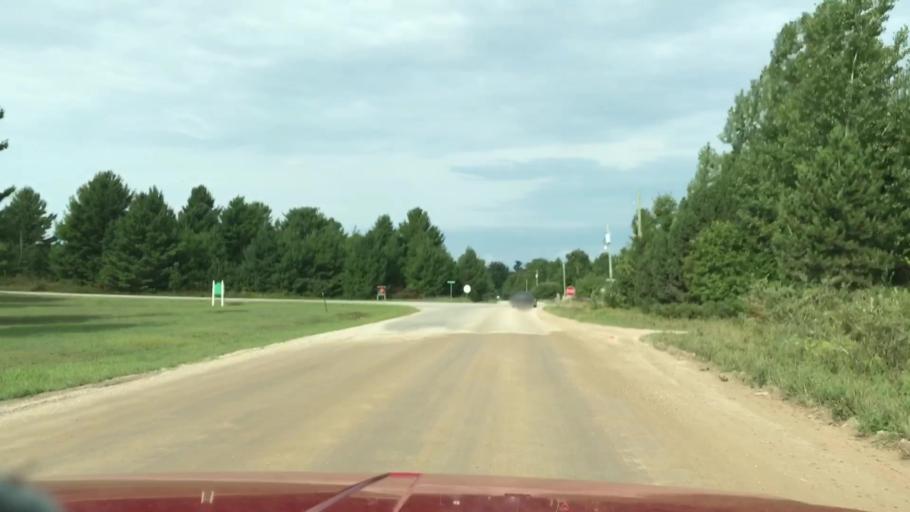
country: US
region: Michigan
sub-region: Charlevoix County
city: Charlevoix
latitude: 45.7286
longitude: -85.5250
